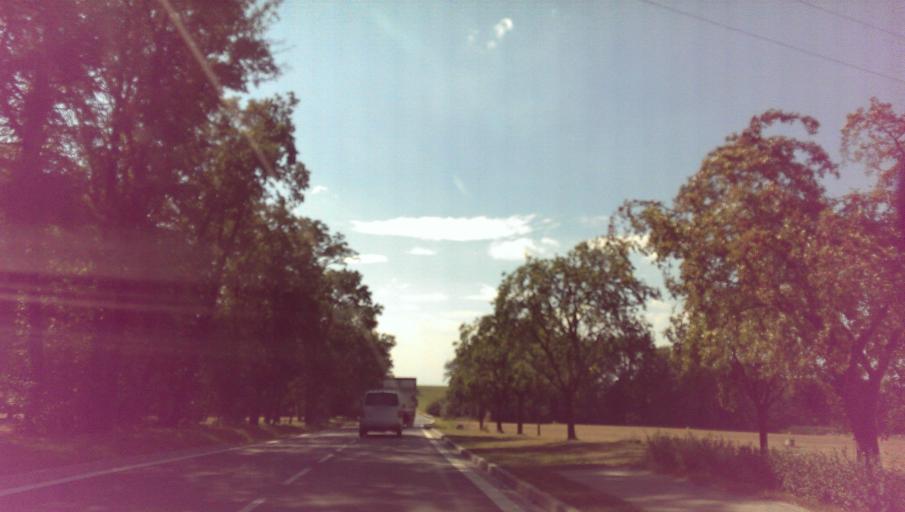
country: CZ
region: Zlin
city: Chvalcov
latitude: 49.4244
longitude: 17.7405
